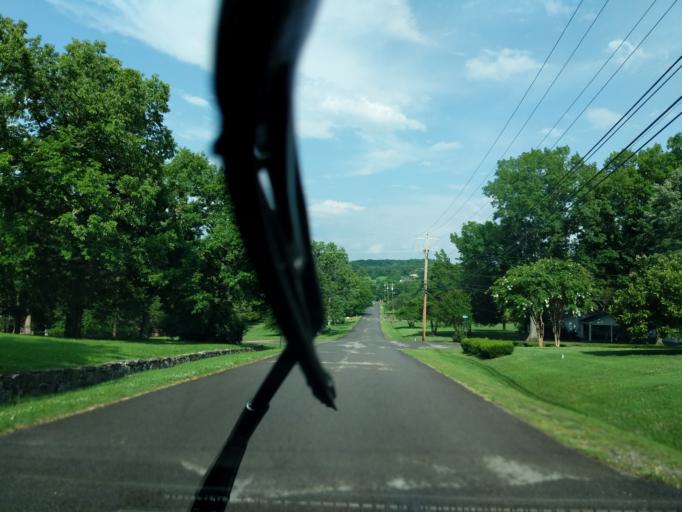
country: US
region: Tennessee
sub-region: Cheatham County
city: Pegram
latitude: 36.0411
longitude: -86.9580
